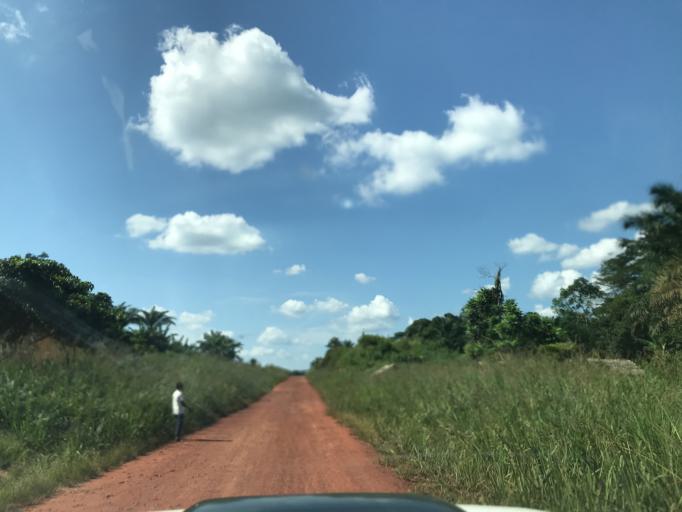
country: CD
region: Eastern Province
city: Kisangani
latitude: 1.2183
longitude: 25.2679
